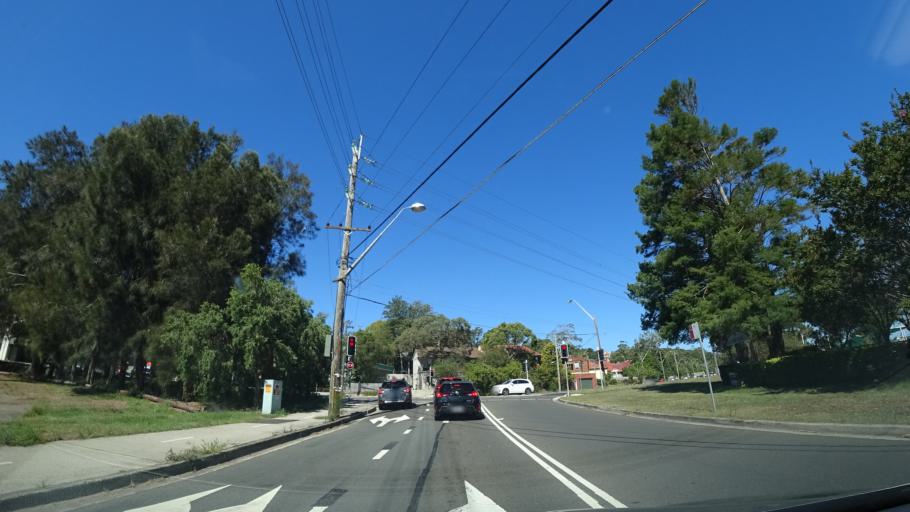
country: AU
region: New South Wales
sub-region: Warringah
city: North Manly
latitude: -33.7755
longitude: 151.2701
